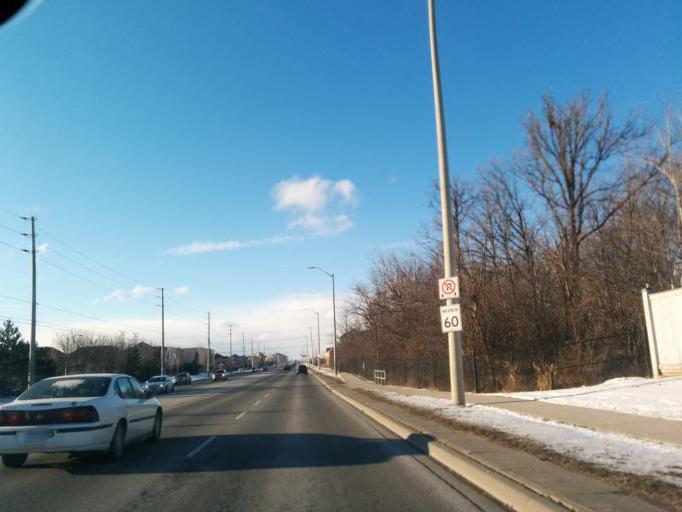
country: CA
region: Ontario
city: Brampton
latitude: 43.6395
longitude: -79.7207
